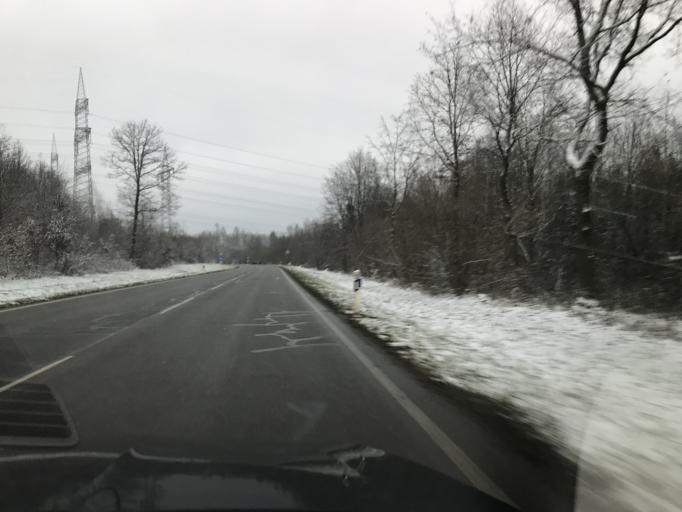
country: DE
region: Baden-Wuerttemberg
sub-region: Regierungsbezirk Stuttgart
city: Altbach
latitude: 48.7390
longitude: 9.3868
